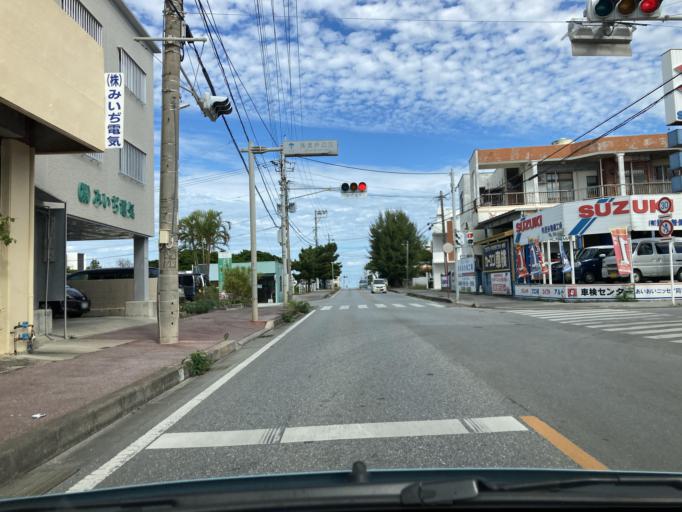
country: JP
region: Okinawa
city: Ishikawa
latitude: 26.4142
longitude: 127.7324
